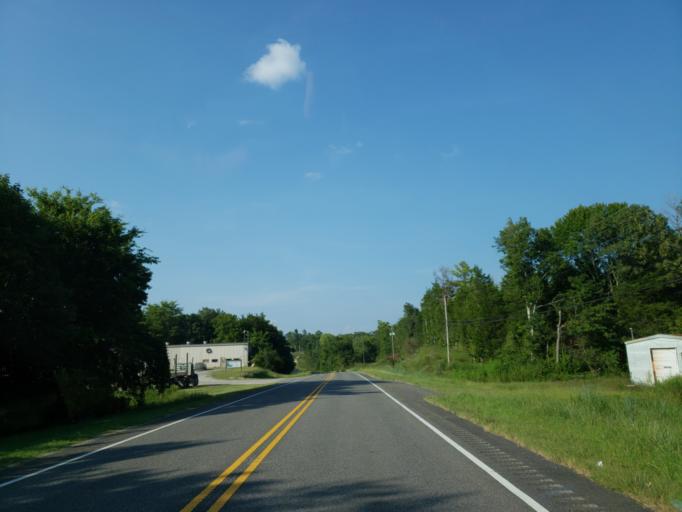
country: US
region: Alabama
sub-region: Sumter County
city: Livingston
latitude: 32.6378
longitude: -88.1730
